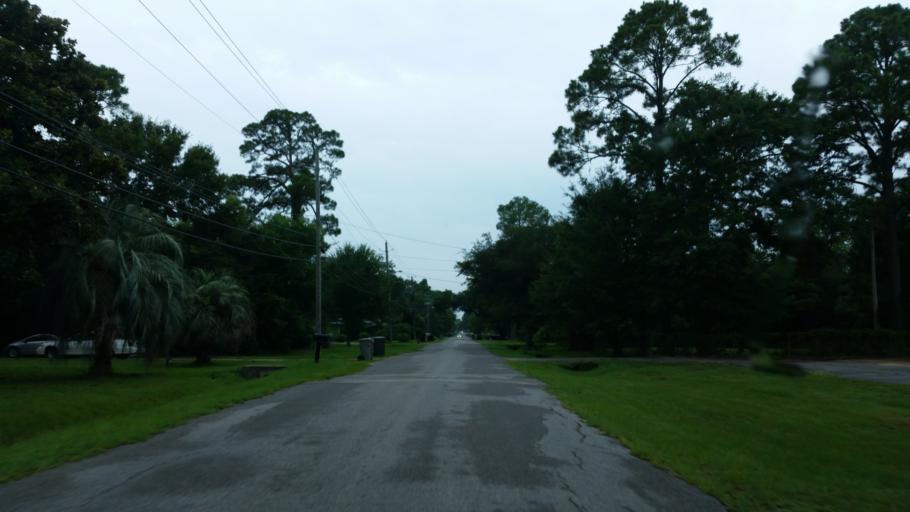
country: US
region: Florida
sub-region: Escambia County
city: Warrington
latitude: 30.3849
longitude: -87.2707
